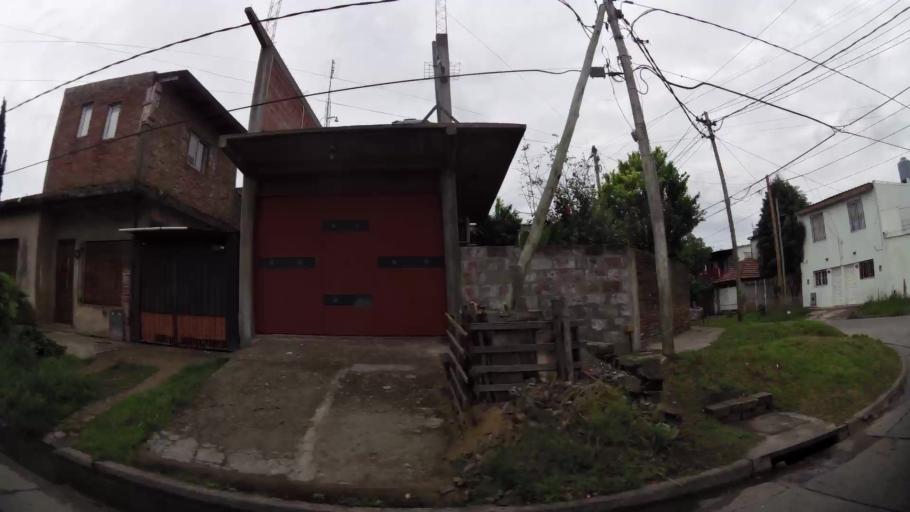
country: AR
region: Buenos Aires
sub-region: Partido de Lanus
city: Lanus
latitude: -34.7317
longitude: -58.3633
